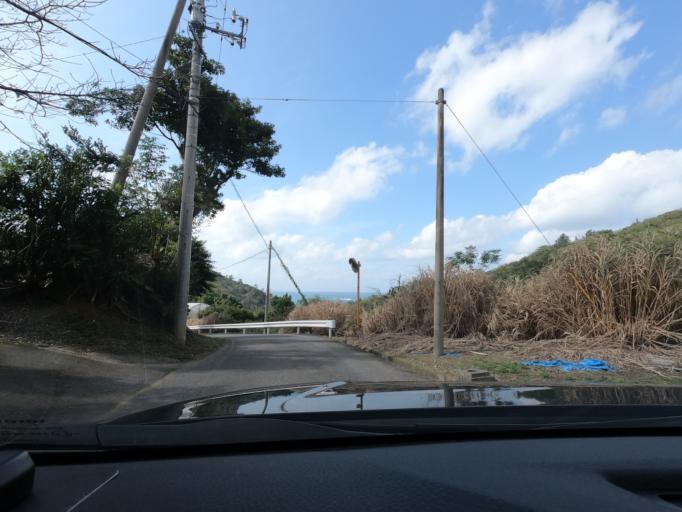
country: JP
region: Okinawa
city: Nago
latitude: 26.7571
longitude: 128.1981
